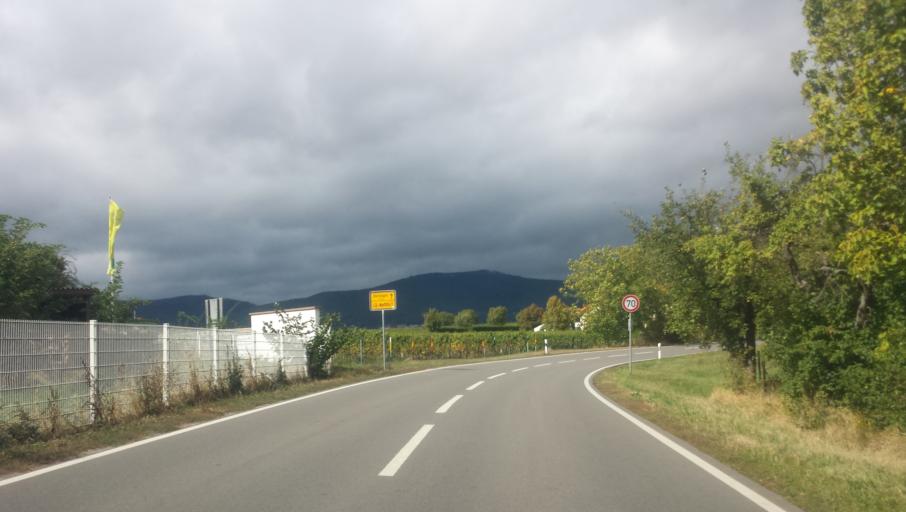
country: DE
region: Rheinland-Pfalz
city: Bochingen
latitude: 49.2230
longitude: 8.1017
